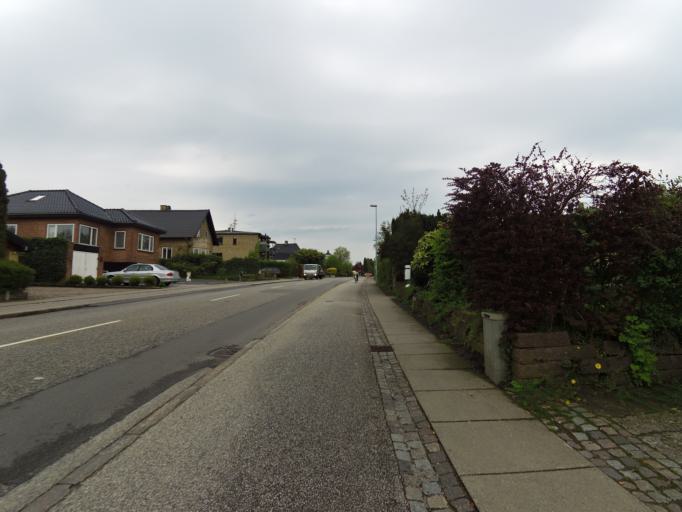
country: DK
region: Capital Region
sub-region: Gladsaxe Municipality
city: Buddinge
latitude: 55.7319
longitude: 12.5218
